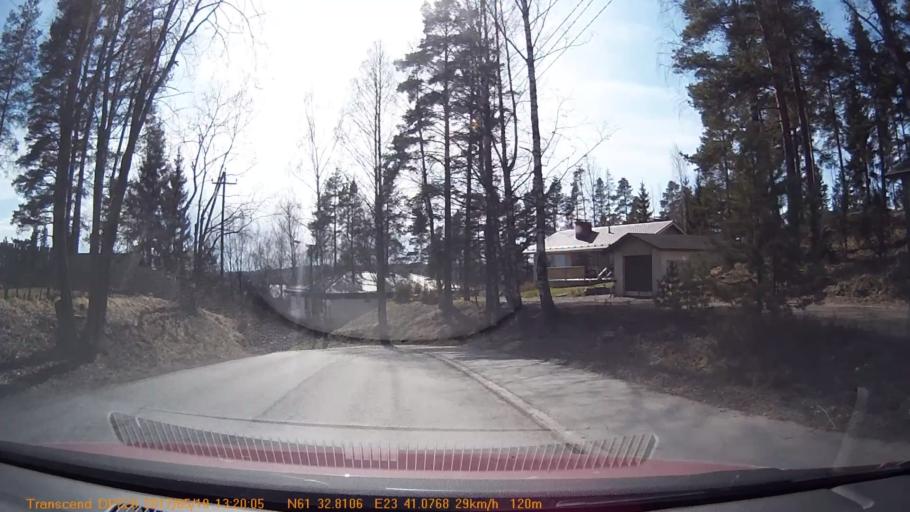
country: FI
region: Pirkanmaa
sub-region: Tampere
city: Yloejaervi
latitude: 61.5469
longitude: 23.6846
